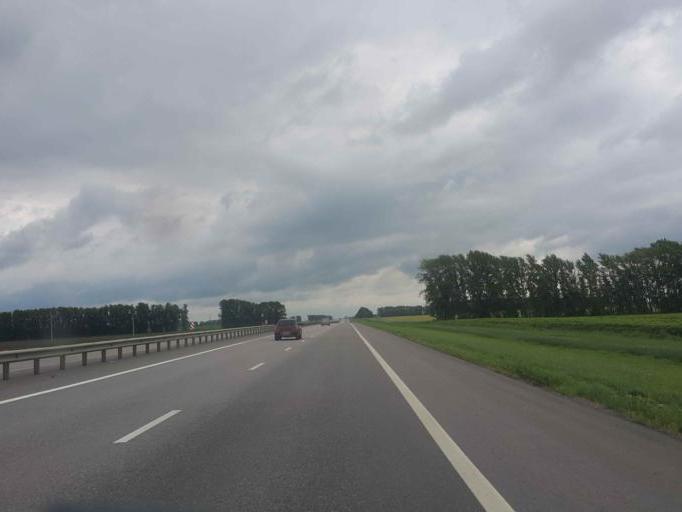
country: RU
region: Tambov
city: Zavoronezhskoye
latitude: 52.8397
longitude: 40.8476
